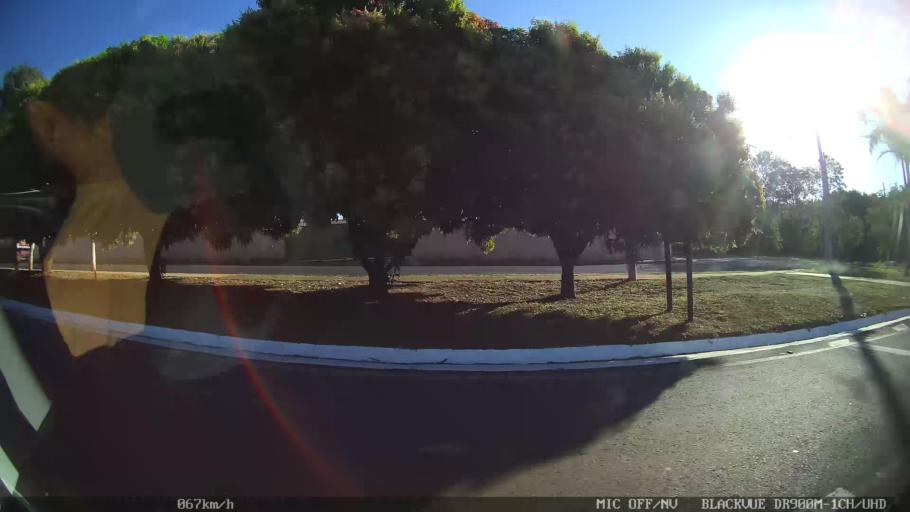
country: BR
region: Sao Paulo
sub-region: Guapiacu
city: Guapiacu
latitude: -20.7873
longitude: -49.2234
